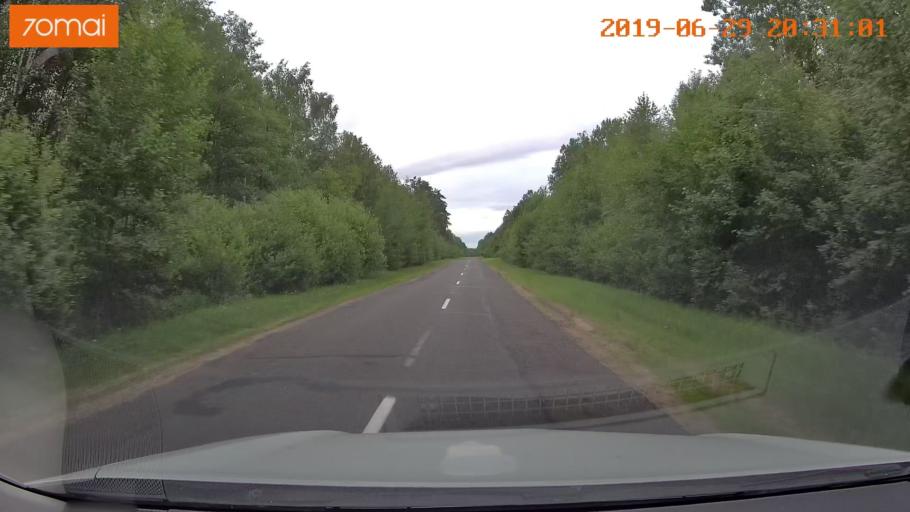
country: BY
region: Brest
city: Hantsavichy
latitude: 52.5105
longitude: 26.3372
